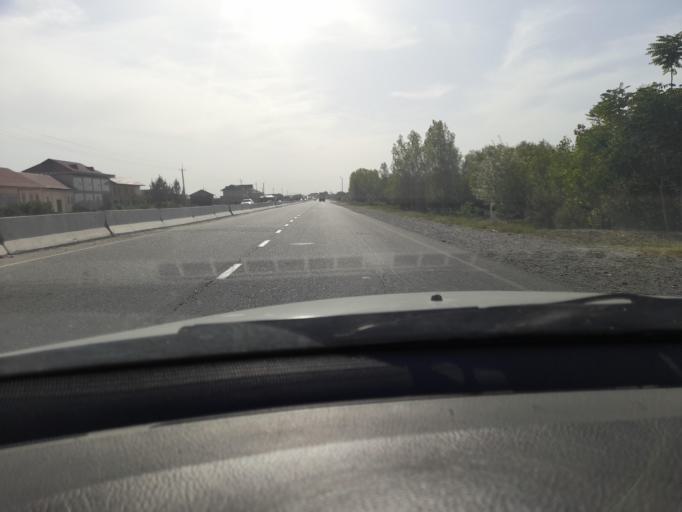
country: UZ
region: Samarqand
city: Kattaqo'rg'on
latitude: 39.9286
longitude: 66.2563
